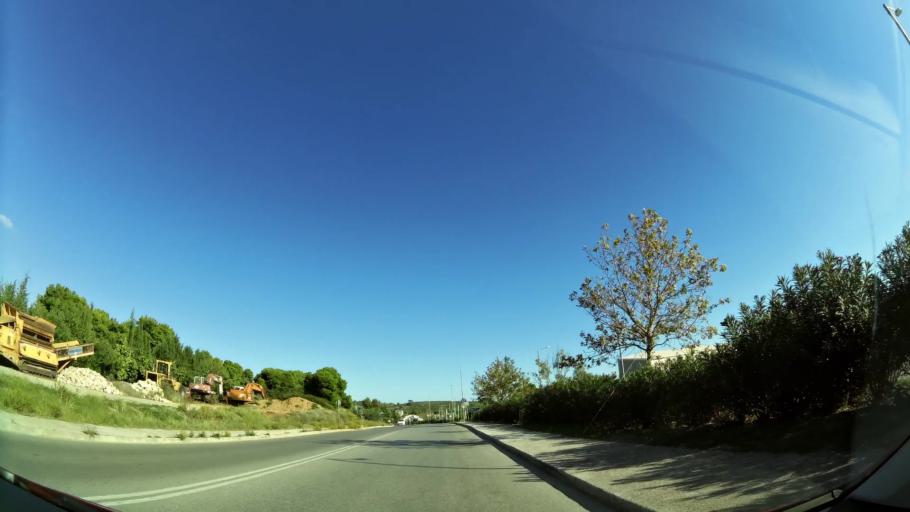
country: GR
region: Attica
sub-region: Nomarchia Anatolikis Attikis
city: Anthousa
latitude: 38.0163
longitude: 23.8691
